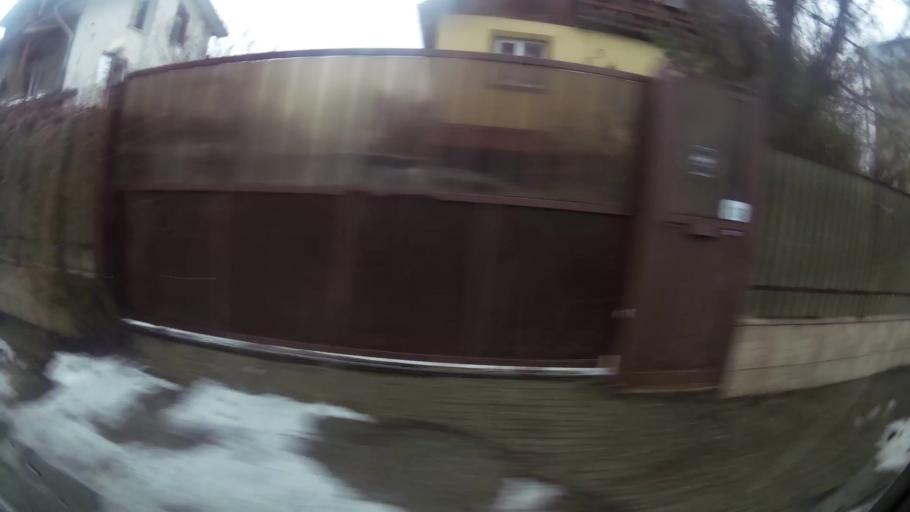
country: RO
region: Ilfov
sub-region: Comuna Chiajna
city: Rosu
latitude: 44.4285
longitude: 26.0125
